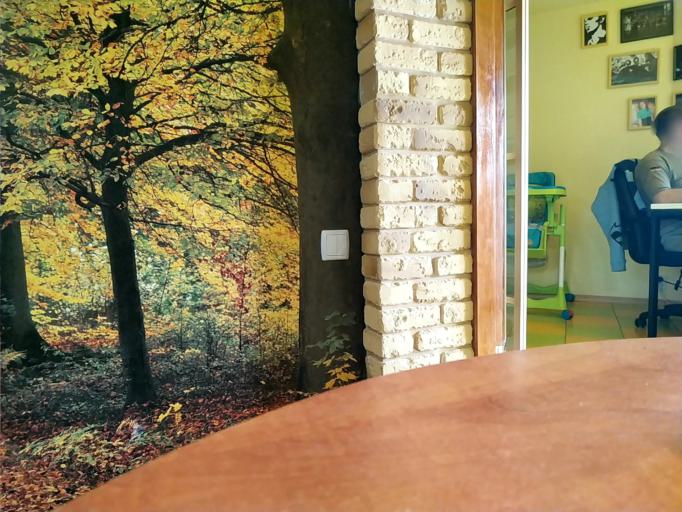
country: RU
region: Tverskaya
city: Vasil'yevskiy Mokh
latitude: 57.1880
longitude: 35.7667
